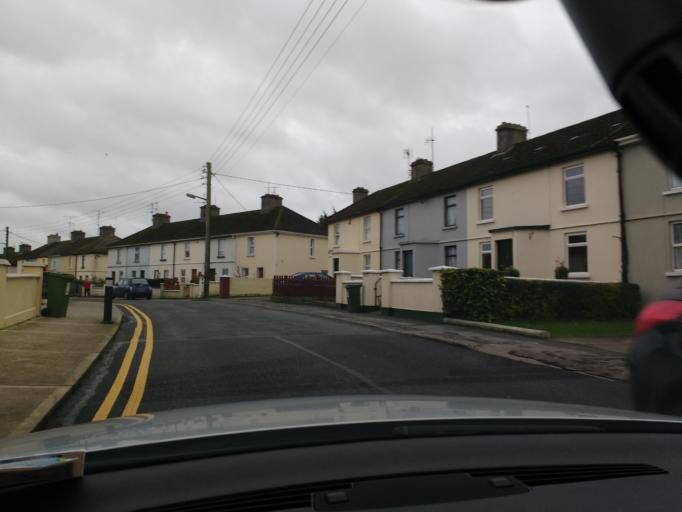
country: IE
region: Munster
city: Thurles
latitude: 52.6756
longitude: -7.8189
